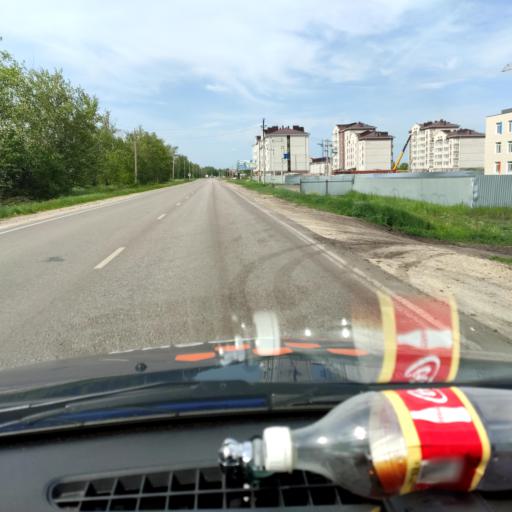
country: RU
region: Voronezj
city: Novaya Usman'
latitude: 51.5993
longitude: 39.3736
